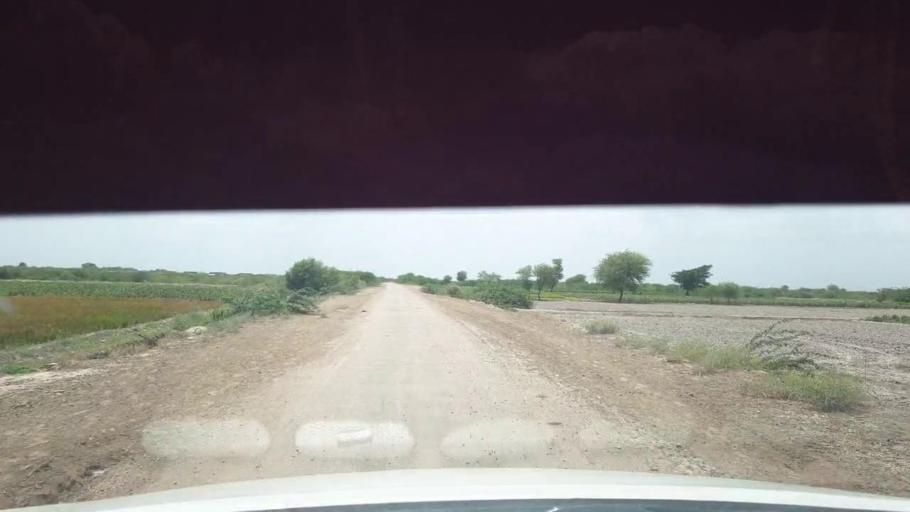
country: PK
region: Sindh
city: Kadhan
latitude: 24.5261
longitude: 69.0949
